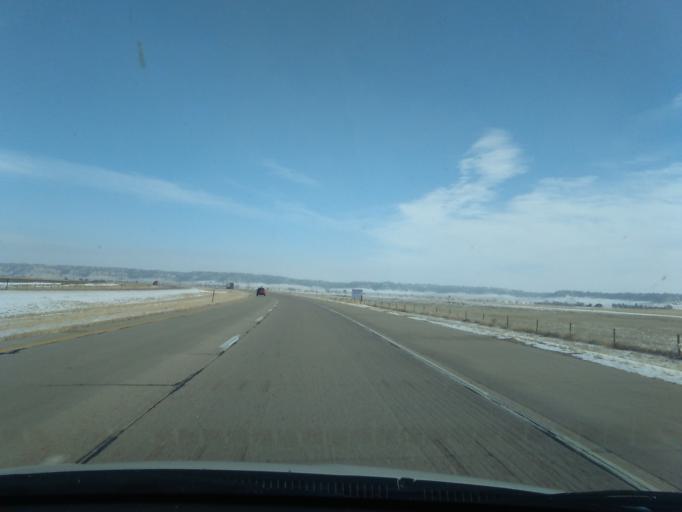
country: US
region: Wyoming
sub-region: Laramie County
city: Pine Bluffs
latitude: 41.1496
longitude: -104.1231
